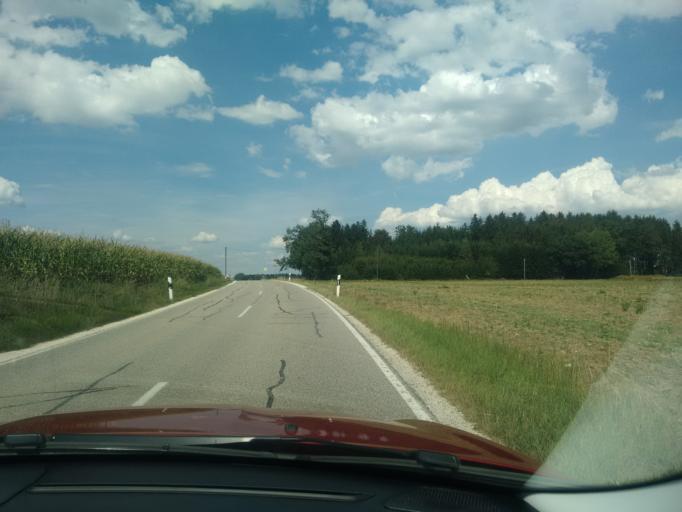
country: DE
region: Bavaria
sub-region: Upper Bavaria
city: Tacherting
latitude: 48.0558
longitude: 12.5932
